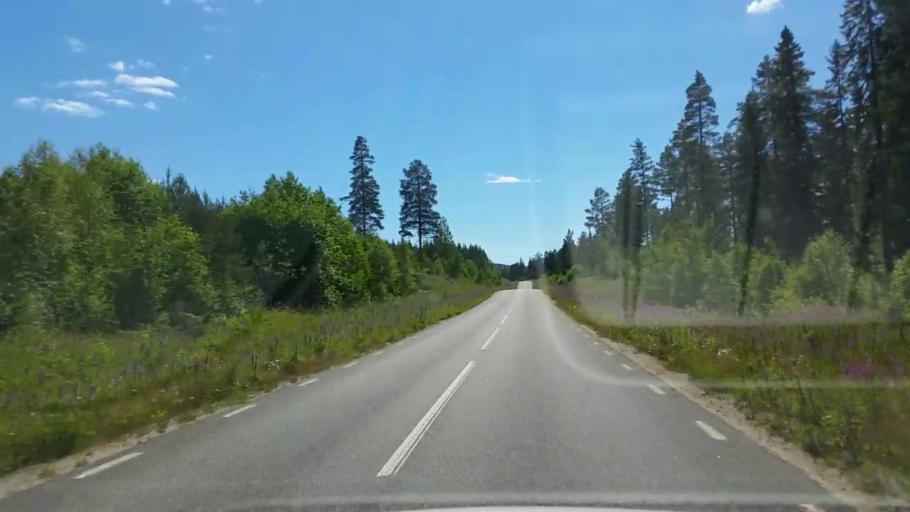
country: SE
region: Gaevleborg
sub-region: Ljusdals Kommun
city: Farila
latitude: 61.7311
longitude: 15.7260
